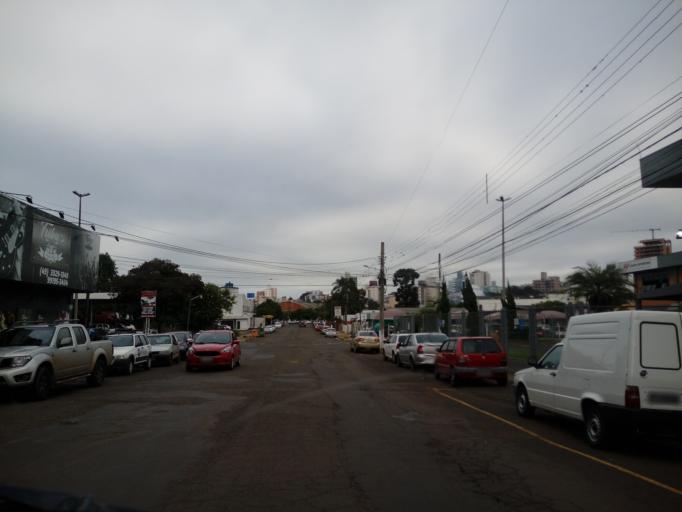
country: BR
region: Santa Catarina
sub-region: Chapeco
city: Chapeco
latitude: -27.0916
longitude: -52.6209
